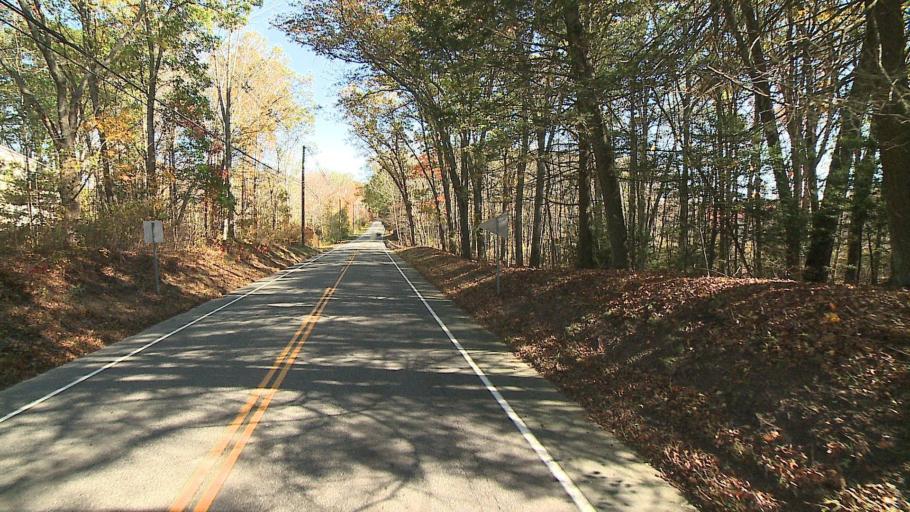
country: US
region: Connecticut
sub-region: Tolland County
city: Storrs
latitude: 41.8473
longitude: -72.2034
